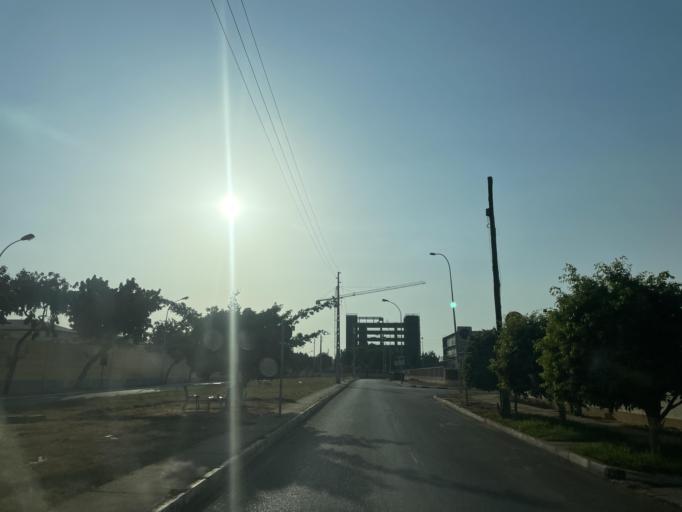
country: AO
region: Luanda
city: Luanda
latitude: -8.9151
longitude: 13.1843
